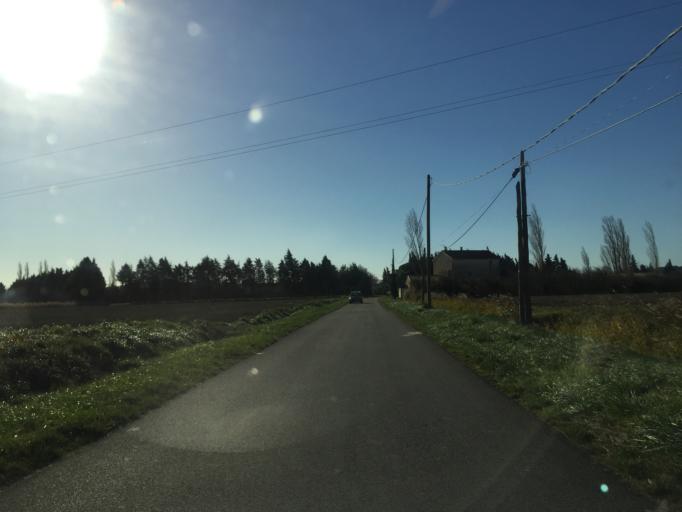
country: FR
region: Provence-Alpes-Cote d'Azur
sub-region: Departement du Vaucluse
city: Bedarrides
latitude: 44.0530
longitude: 4.9042
